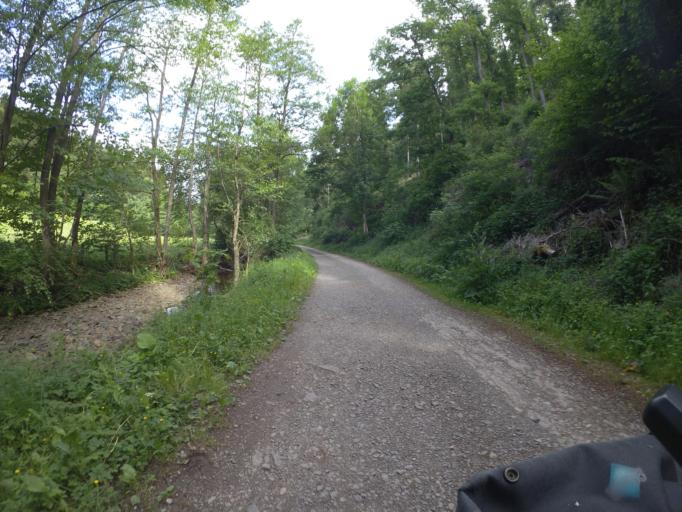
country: DE
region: North Rhine-Westphalia
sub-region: Regierungsbezirk Koln
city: Hellenthal
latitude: 50.4594
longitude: 6.4249
